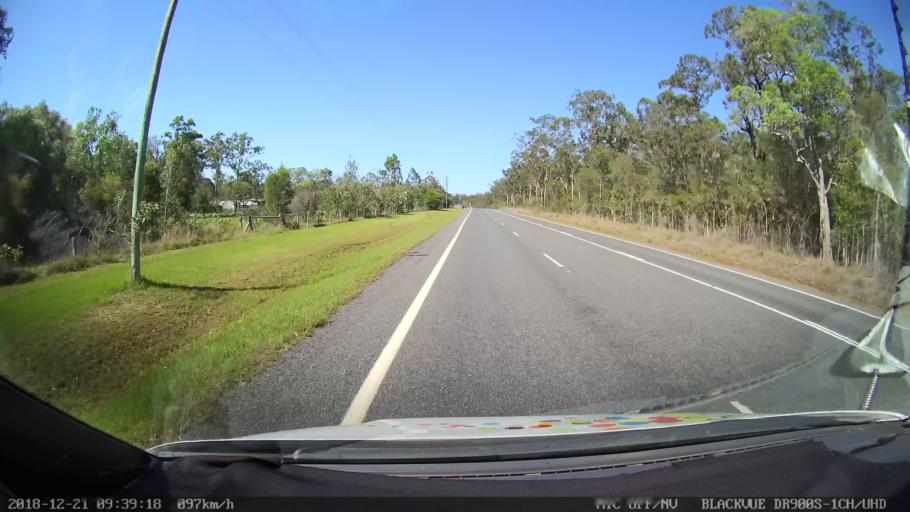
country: AU
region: New South Wales
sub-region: Clarence Valley
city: Grafton
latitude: -29.5596
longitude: 152.9741
